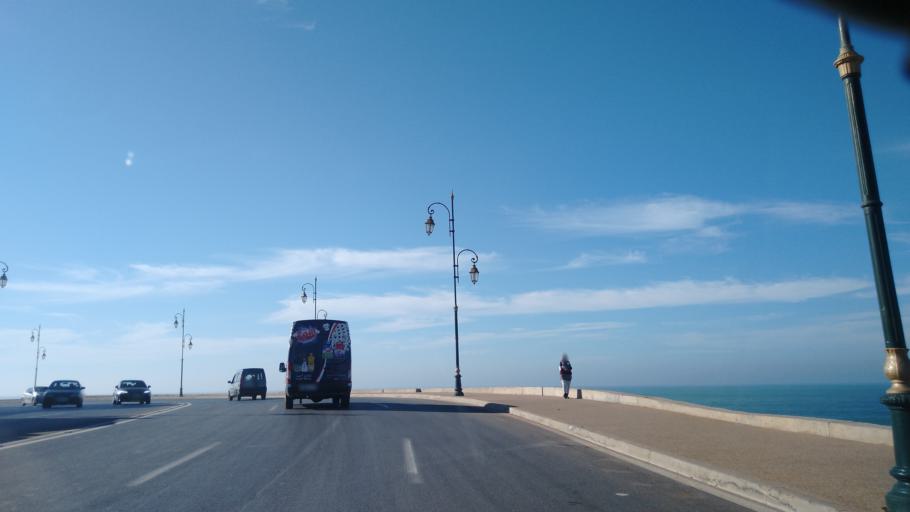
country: MA
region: Rabat-Sale-Zemmour-Zaer
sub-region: Rabat
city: Rabat
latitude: 34.0216
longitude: -6.8544
